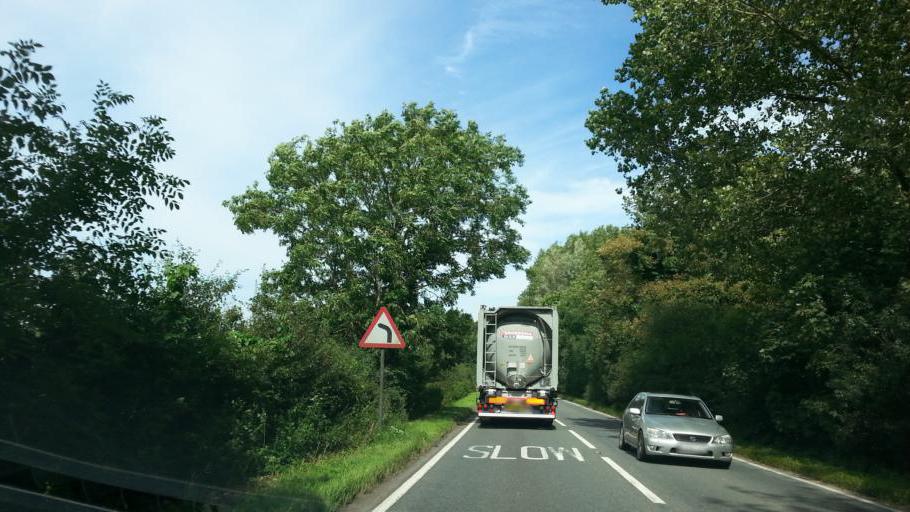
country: GB
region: England
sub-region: Suffolk
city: Exning
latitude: 52.2748
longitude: 0.3938
